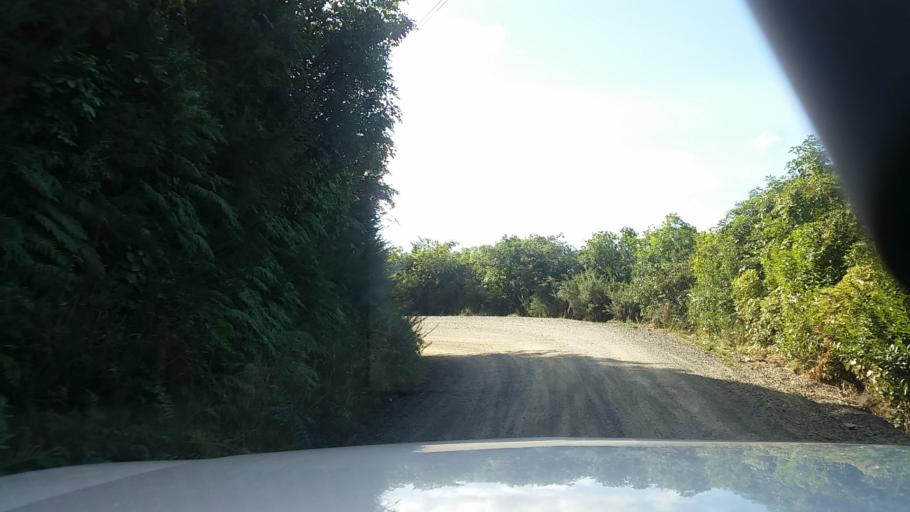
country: NZ
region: Marlborough
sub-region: Marlborough District
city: Picton
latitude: -41.2949
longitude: 174.1243
